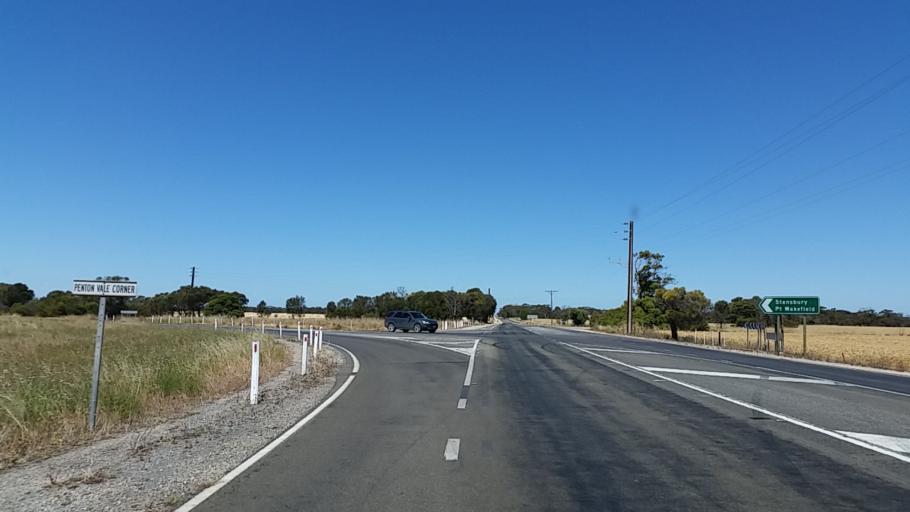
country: AU
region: South Australia
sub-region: Yorke Peninsula
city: Honiton
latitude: -35.0134
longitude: 137.6626
